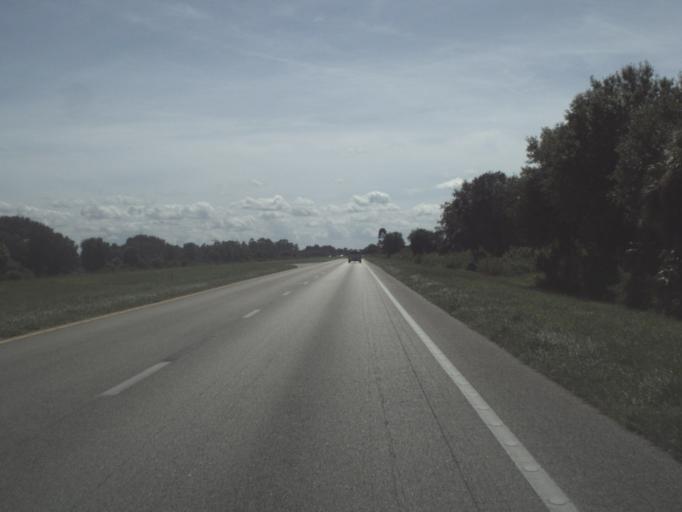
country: US
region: Florida
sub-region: Hendry County
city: Port LaBelle
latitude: 26.9872
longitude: -81.3241
